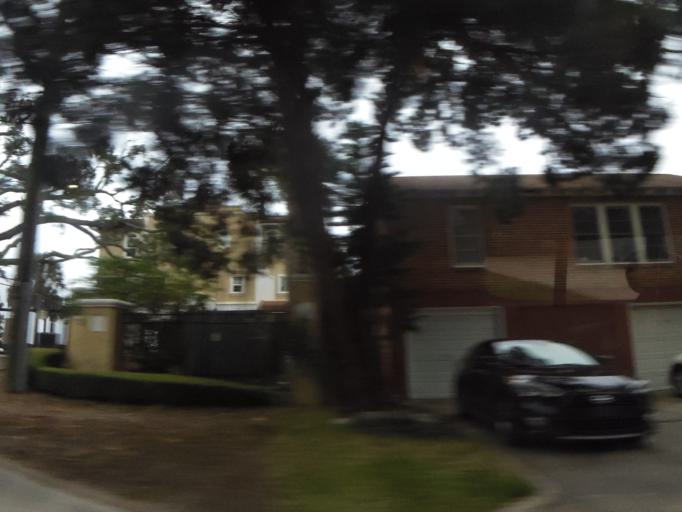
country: US
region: Florida
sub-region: Duval County
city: Jacksonville
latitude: 30.3084
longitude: -81.6616
